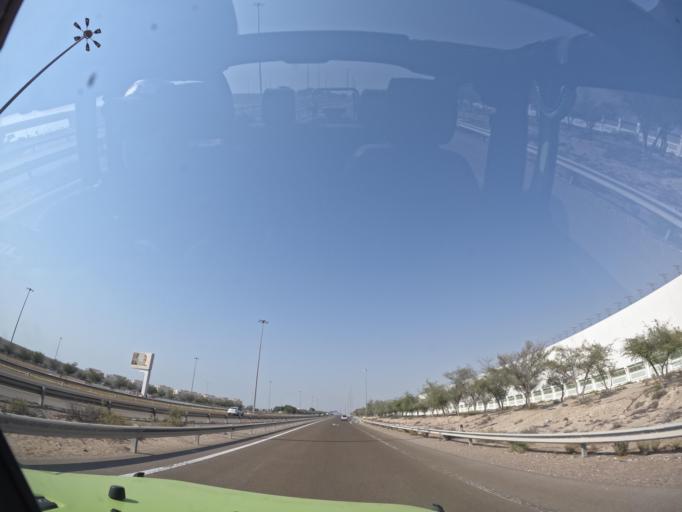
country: AE
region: Abu Dhabi
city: Abu Dhabi
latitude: 24.5459
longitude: 54.6944
